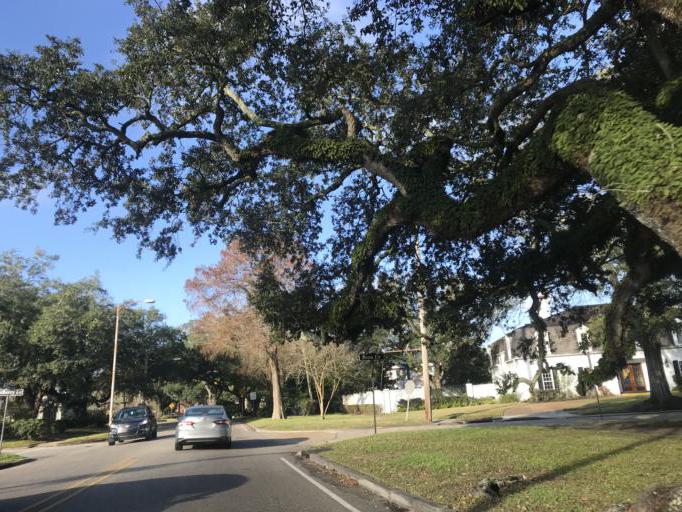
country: US
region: Louisiana
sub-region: Jefferson Parish
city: Metairie
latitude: 29.9890
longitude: -90.1357
